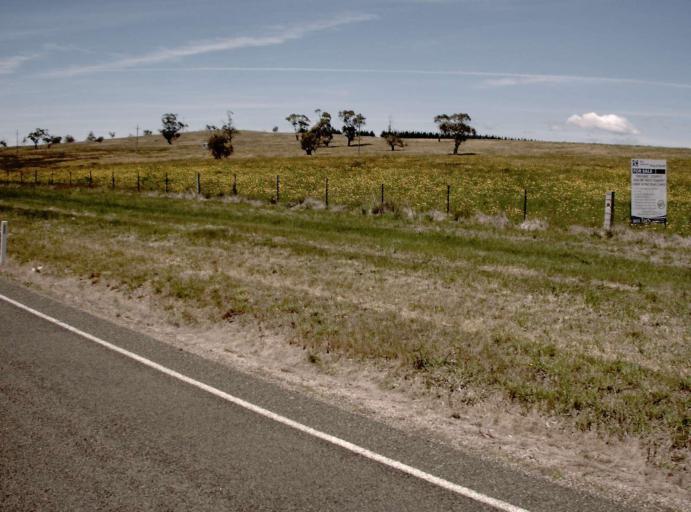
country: AU
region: Victoria
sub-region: Alpine
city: Mount Beauty
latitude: -37.1275
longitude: 147.6393
